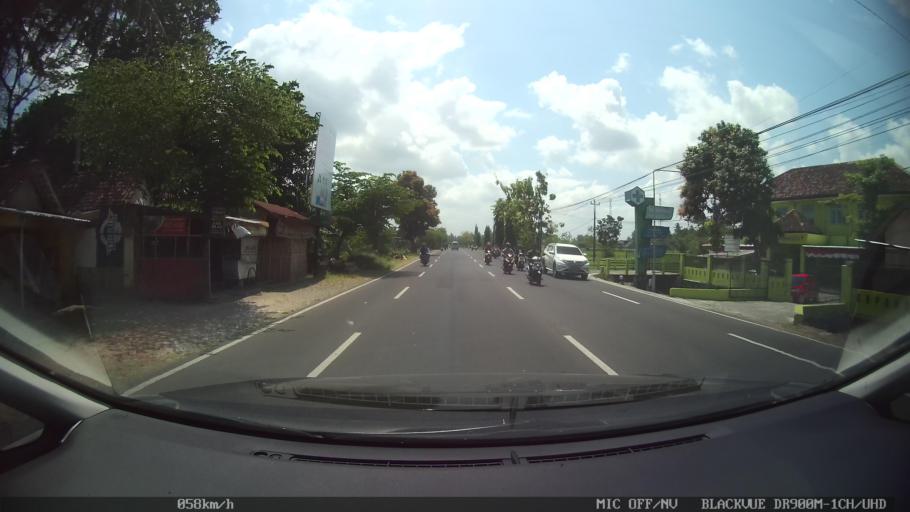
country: ID
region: Daerah Istimewa Yogyakarta
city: Pandak
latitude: -7.9187
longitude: 110.2834
